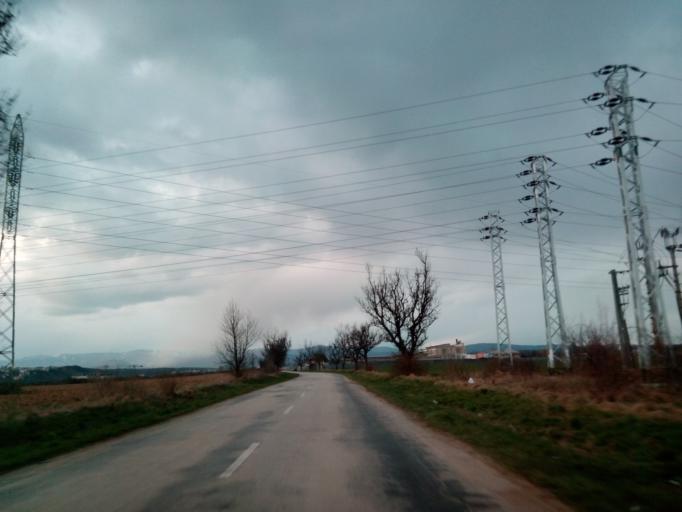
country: SK
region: Kosicky
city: Moldava nad Bodvou
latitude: 48.5946
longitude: 20.9964
